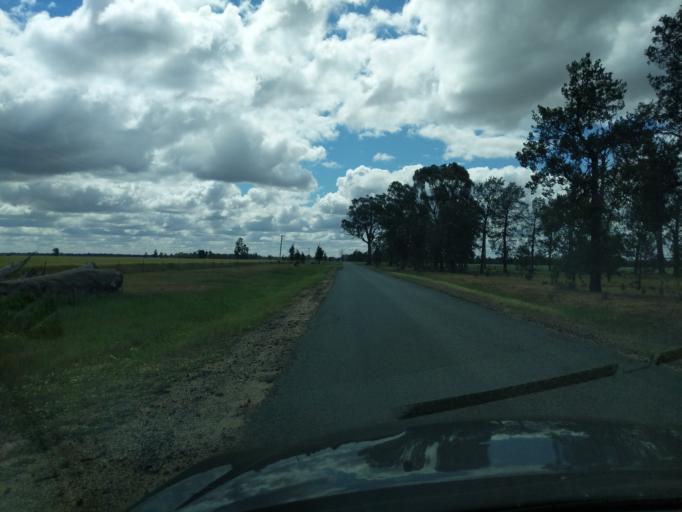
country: AU
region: New South Wales
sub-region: Coolamon
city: Coolamon
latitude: -34.8629
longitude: 146.8974
